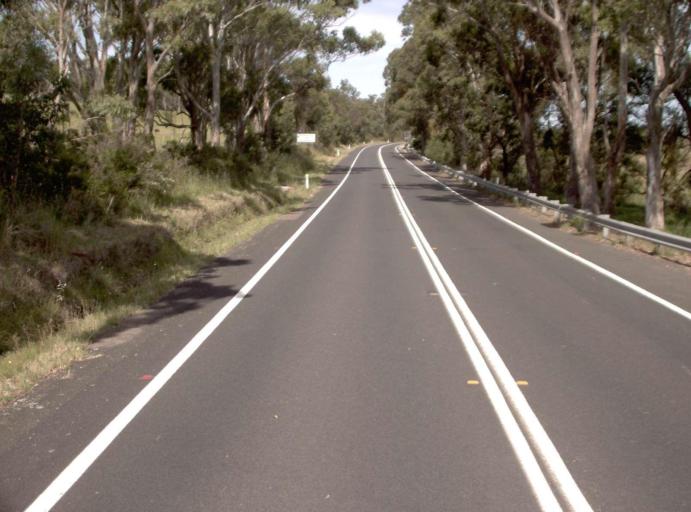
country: AU
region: Victoria
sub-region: East Gippsland
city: Lakes Entrance
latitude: -37.8243
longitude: 147.8803
